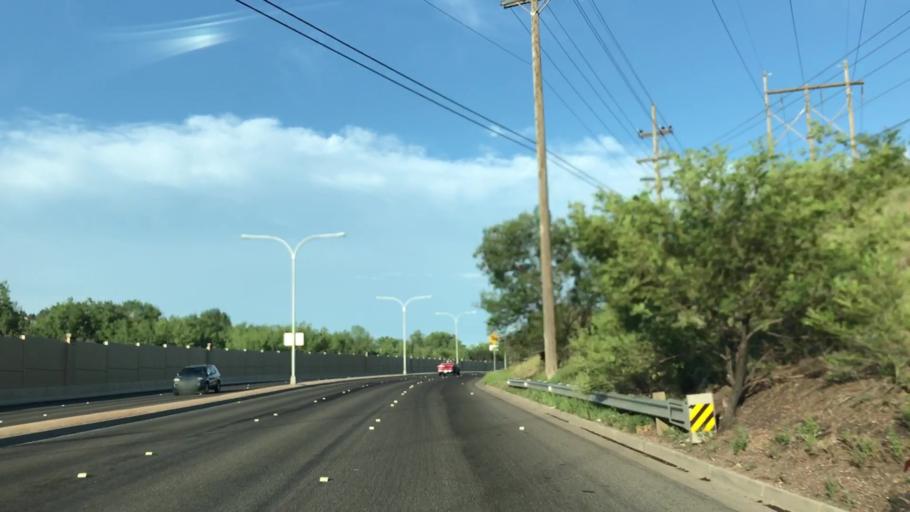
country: US
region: Colorado
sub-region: El Paso County
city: Colorado Springs
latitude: 38.8892
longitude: -104.7809
